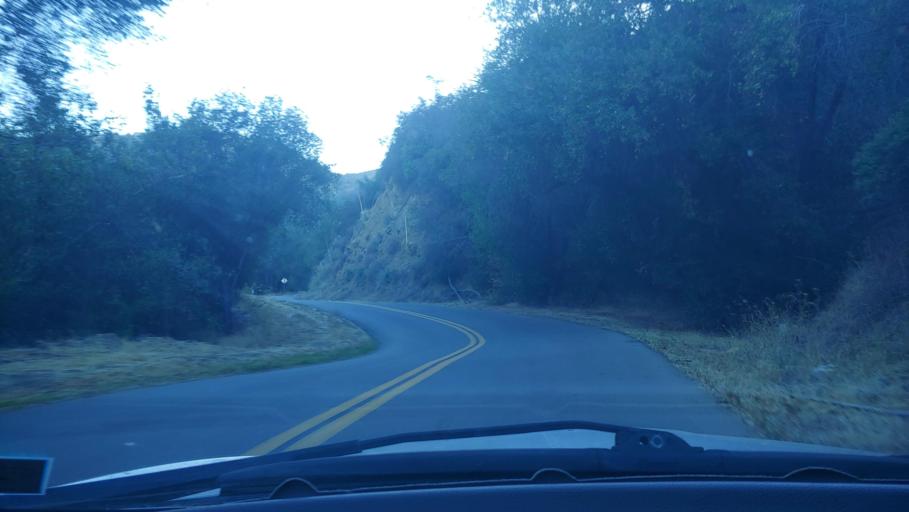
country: US
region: California
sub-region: Santa Barbara County
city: Goleta
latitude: 34.5257
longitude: -119.8361
